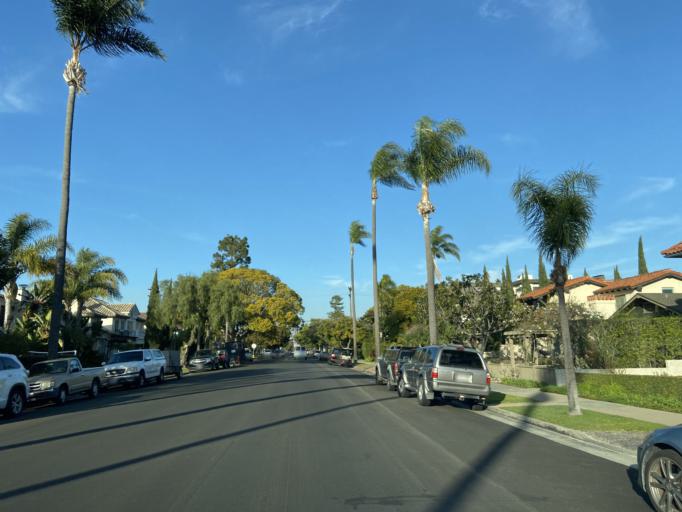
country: US
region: California
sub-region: San Diego County
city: Coronado
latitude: 32.6893
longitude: -117.1736
